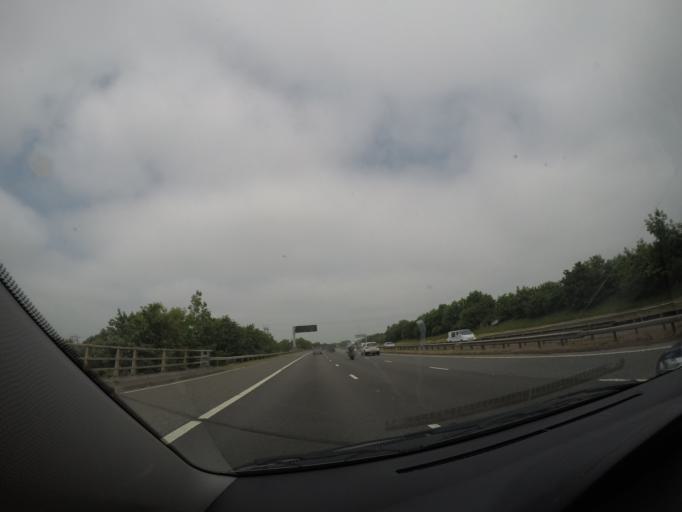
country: GB
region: England
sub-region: North Yorkshire
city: Boroughbridge
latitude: 54.1000
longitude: -1.4124
